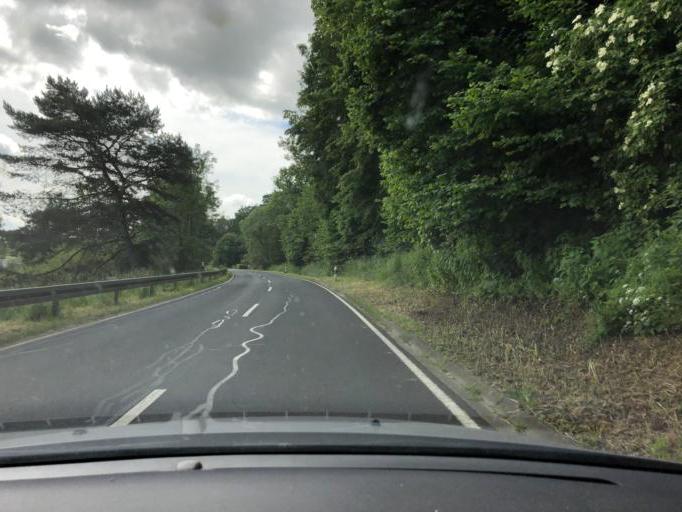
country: DE
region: Hesse
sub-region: Regierungsbezirk Kassel
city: Alheim
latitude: 51.0518
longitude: 9.6158
